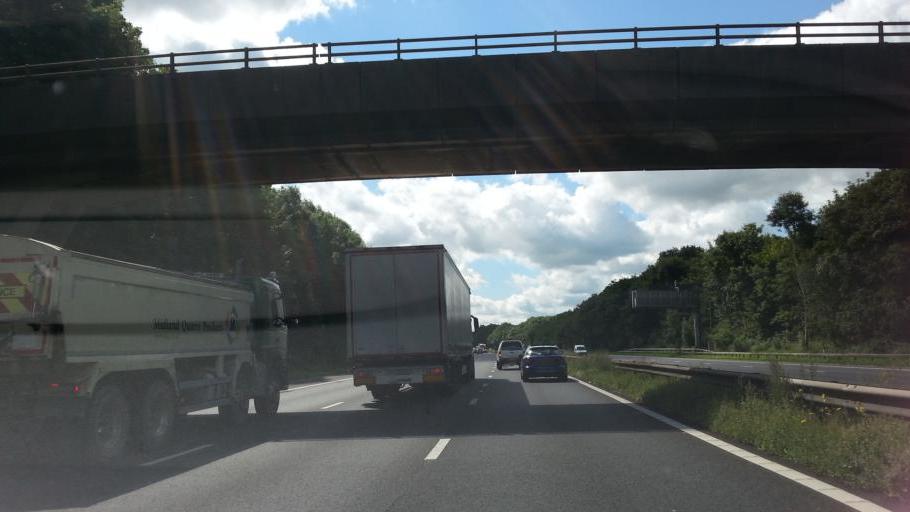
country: GB
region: England
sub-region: Leicestershire
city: Lutterworth
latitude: 52.4918
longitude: -1.1915
